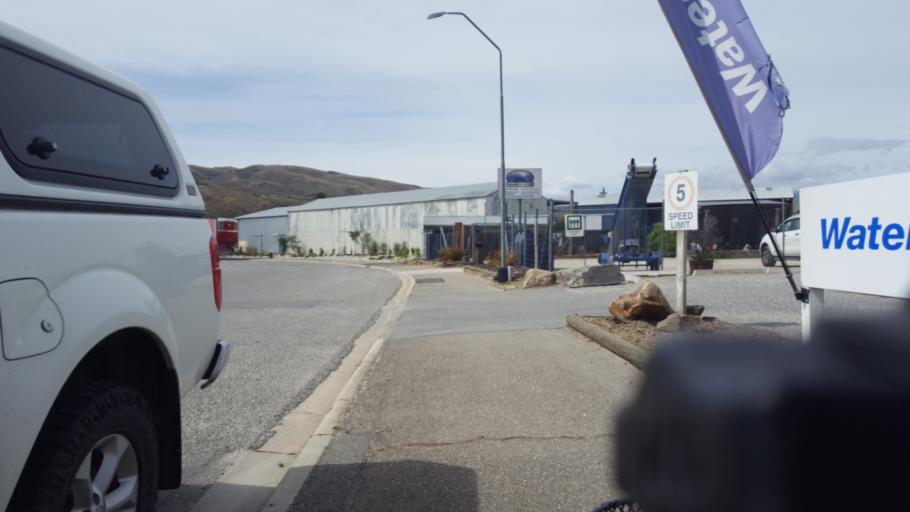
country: NZ
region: Otago
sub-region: Queenstown-Lakes District
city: Wanaka
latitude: -45.0523
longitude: 169.1939
